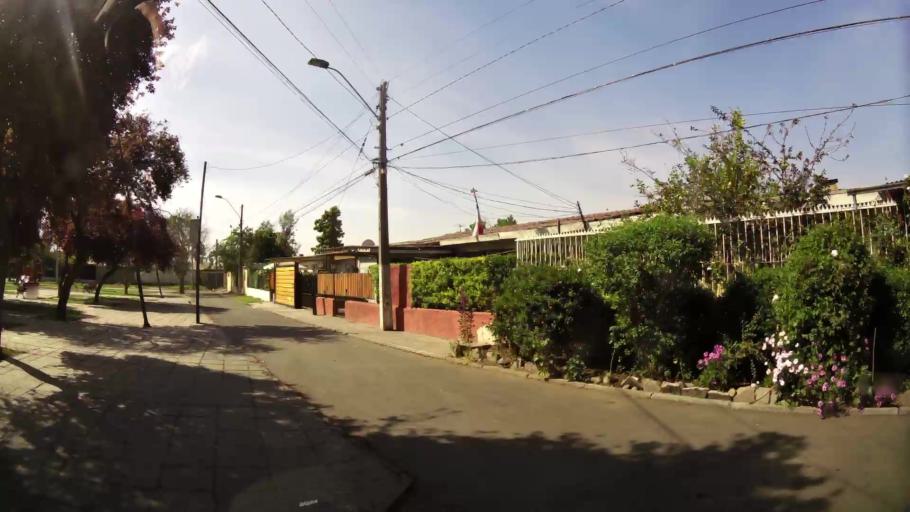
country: CL
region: Santiago Metropolitan
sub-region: Provincia de Santiago
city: La Pintana
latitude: -33.5413
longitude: -70.6260
